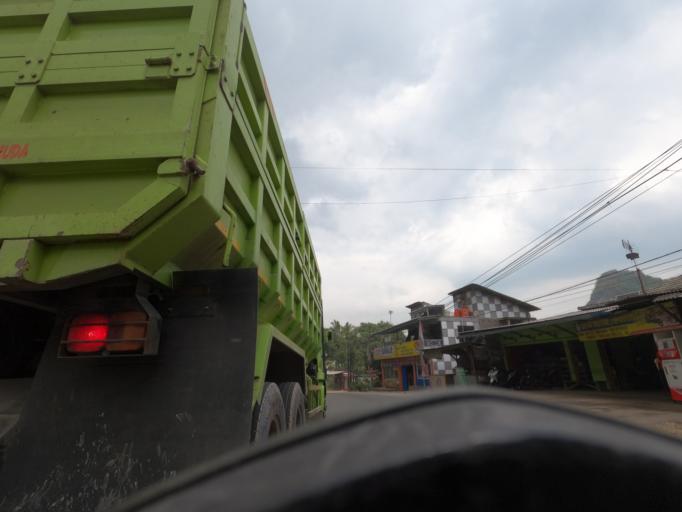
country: ID
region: West Java
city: Padalarang
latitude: -6.8313
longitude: 107.4301
